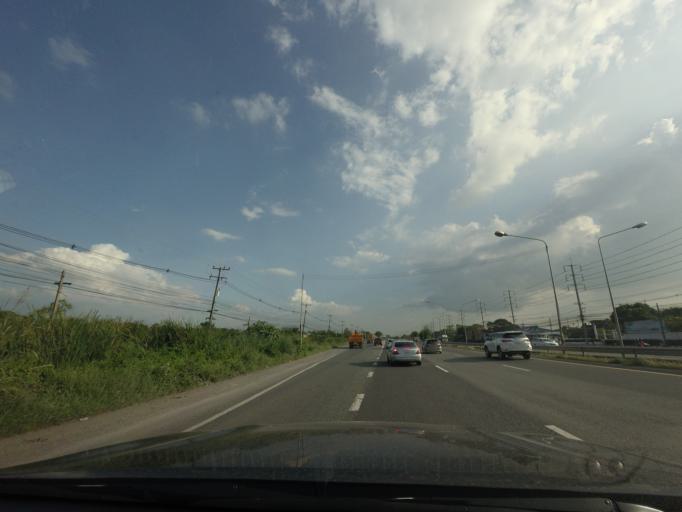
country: TH
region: Sara Buri
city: Saraburi
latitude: 14.5694
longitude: 100.9033
